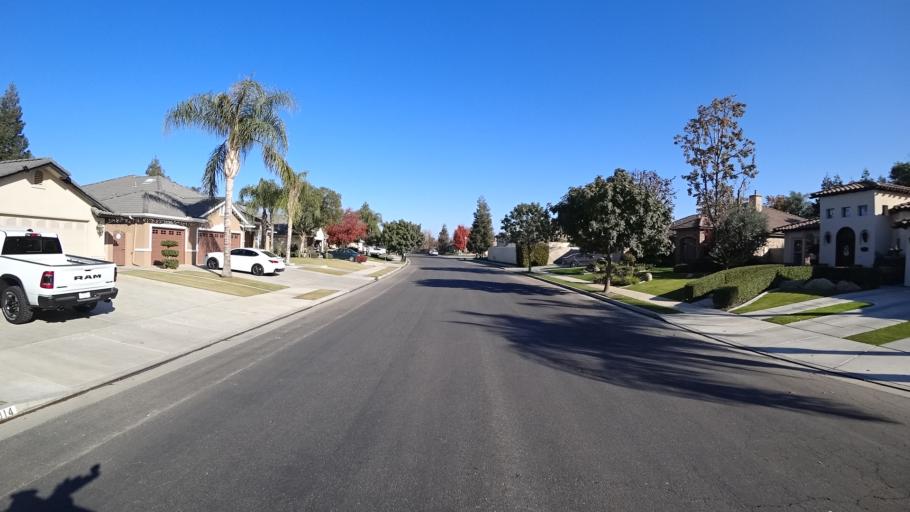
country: US
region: California
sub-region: Kern County
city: Rosedale
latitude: 35.3258
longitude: -119.1358
